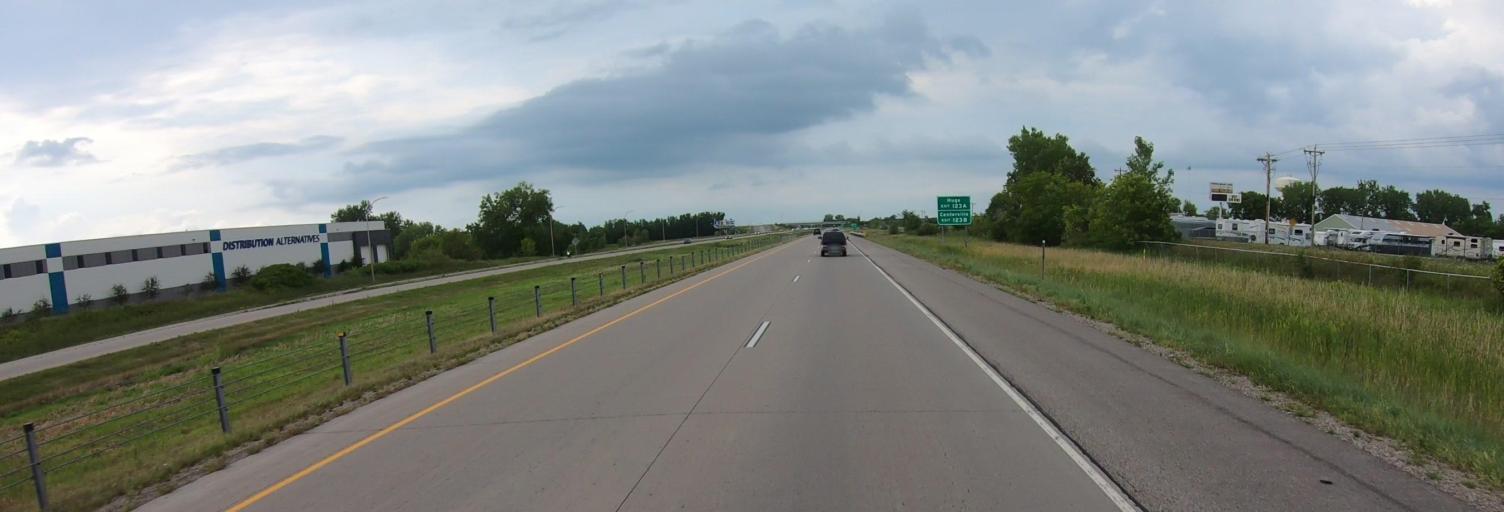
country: US
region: Minnesota
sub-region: Anoka County
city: Centerville
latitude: 45.1549
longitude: -93.0310
